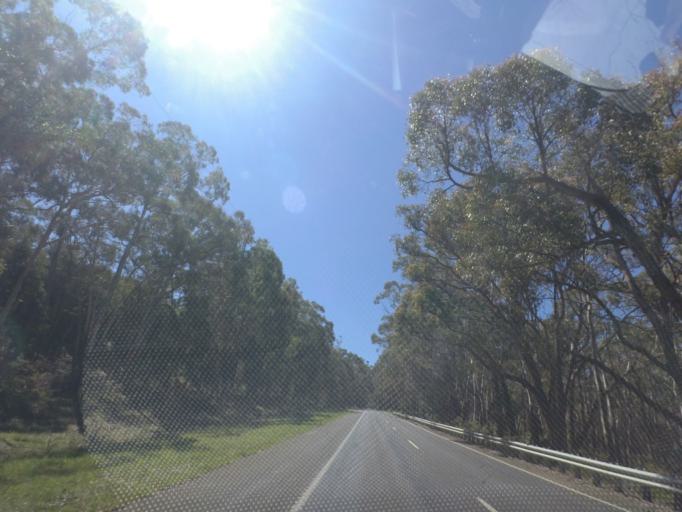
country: AU
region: Victoria
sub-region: Hume
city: Sunbury
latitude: -37.2305
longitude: 144.7406
